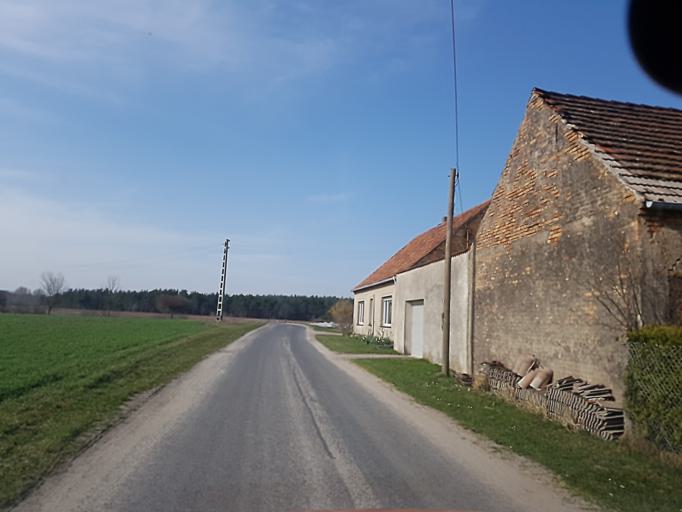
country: DE
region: Brandenburg
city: Bronkow
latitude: 51.6418
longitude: 13.8667
